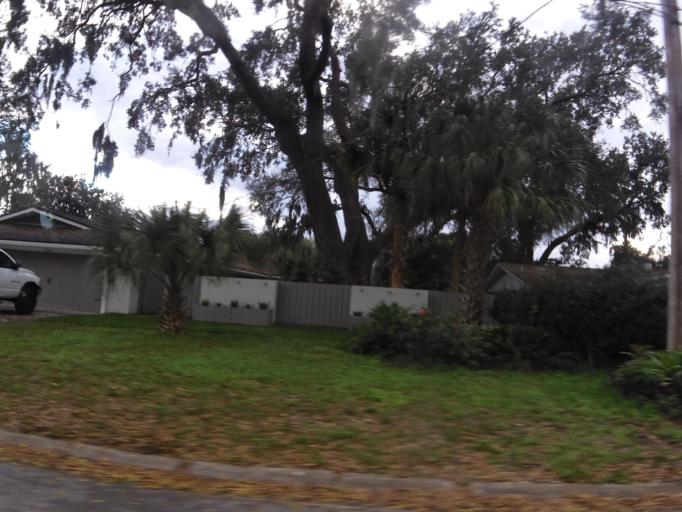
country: US
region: Florida
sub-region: Duval County
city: Jacksonville
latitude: 30.2521
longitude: -81.6367
